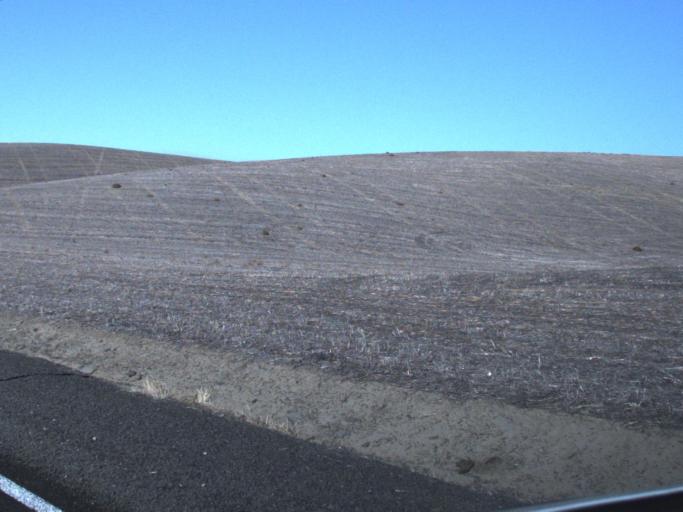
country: US
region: Washington
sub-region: Walla Walla County
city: Walla Walla
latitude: 46.1252
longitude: -118.3727
